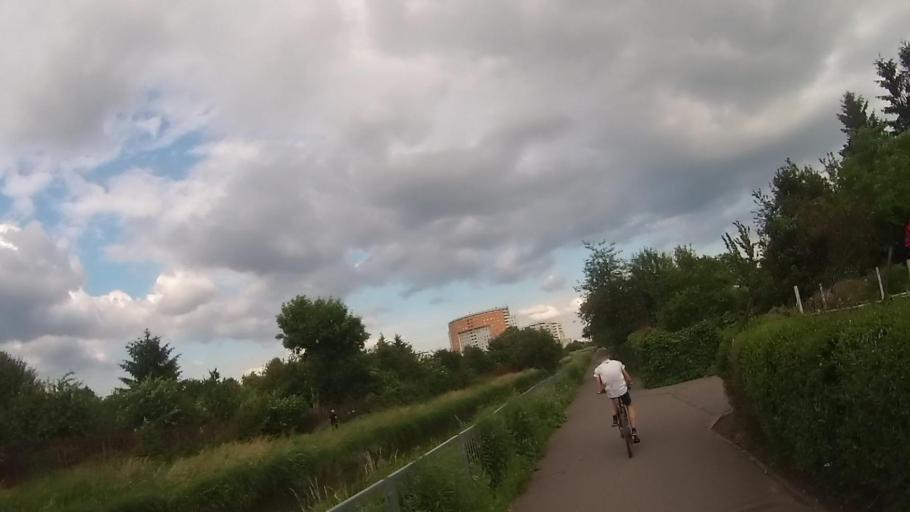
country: PL
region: Masovian Voivodeship
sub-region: Warszawa
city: Praga Poludnie
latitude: 52.2340
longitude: 21.0701
